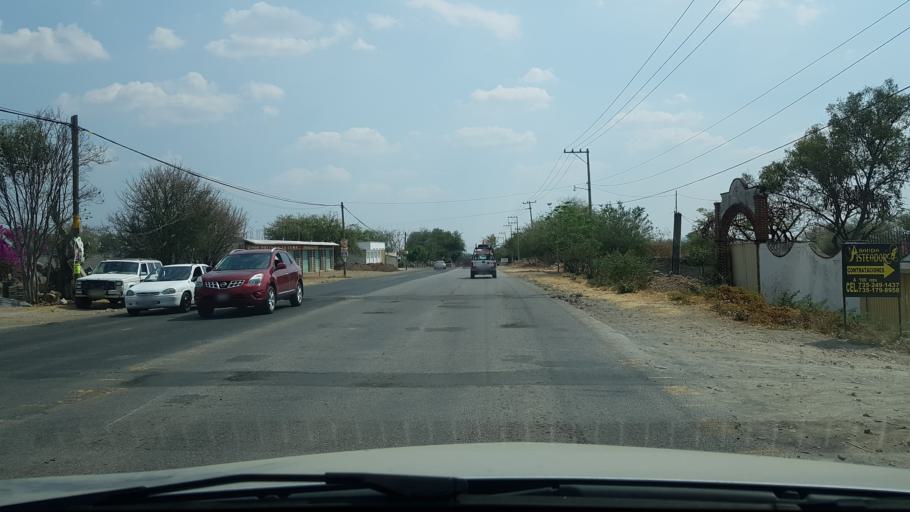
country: MX
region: Morelos
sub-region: Temoac
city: Huazulco
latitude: 18.7512
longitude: -98.7816
